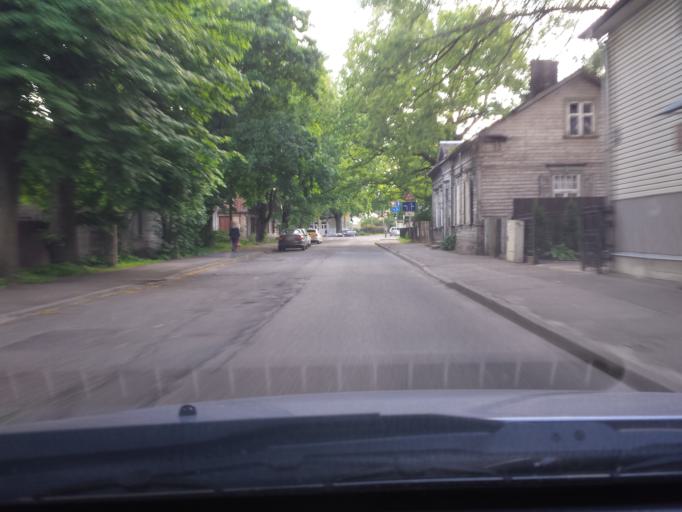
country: LV
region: Riga
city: Riga
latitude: 56.9605
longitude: 24.0548
